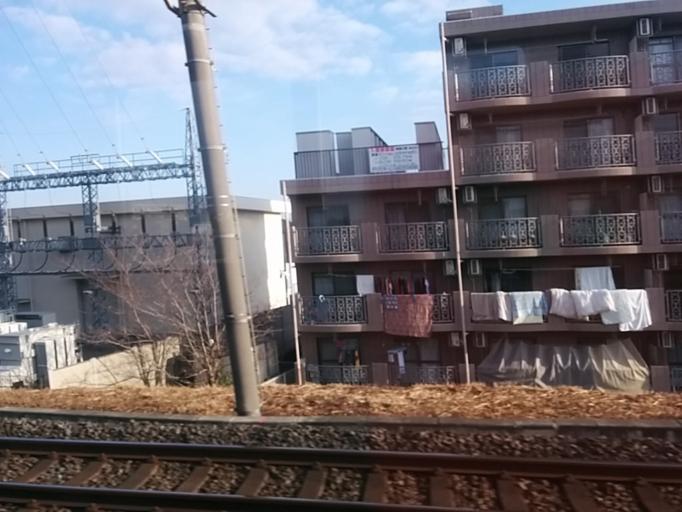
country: JP
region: Saitama
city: Shiki
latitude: 35.8327
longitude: 139.5592
